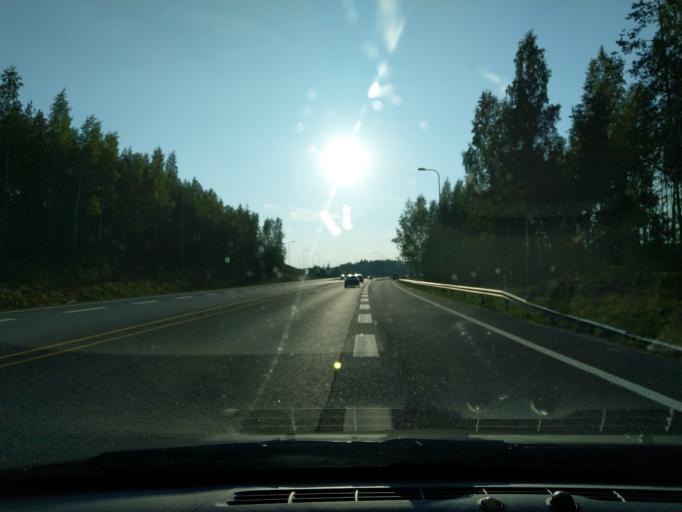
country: FI
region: Paijanne Tavastia
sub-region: Lahti
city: Lahti
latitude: 60.9678
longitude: 25.7330
